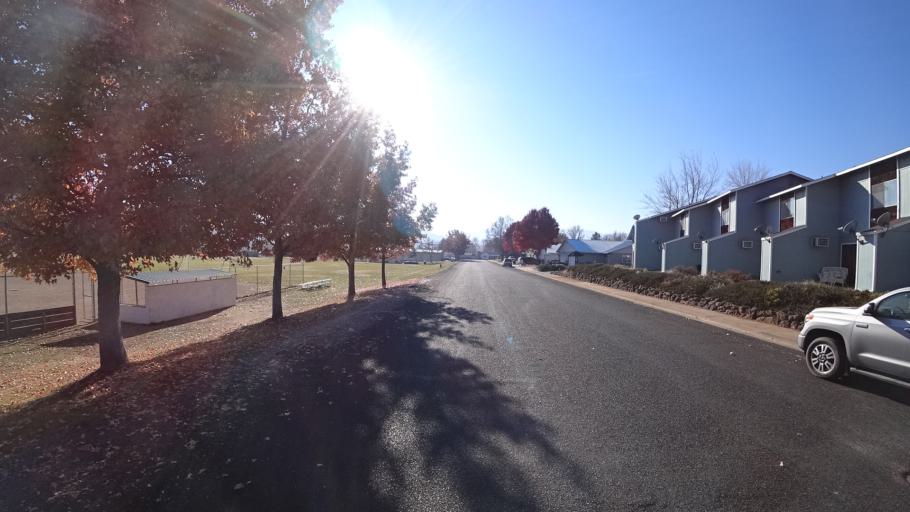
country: US
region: California
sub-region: Siskiyou County
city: Yreka
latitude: 41.7258
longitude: -122.6461
